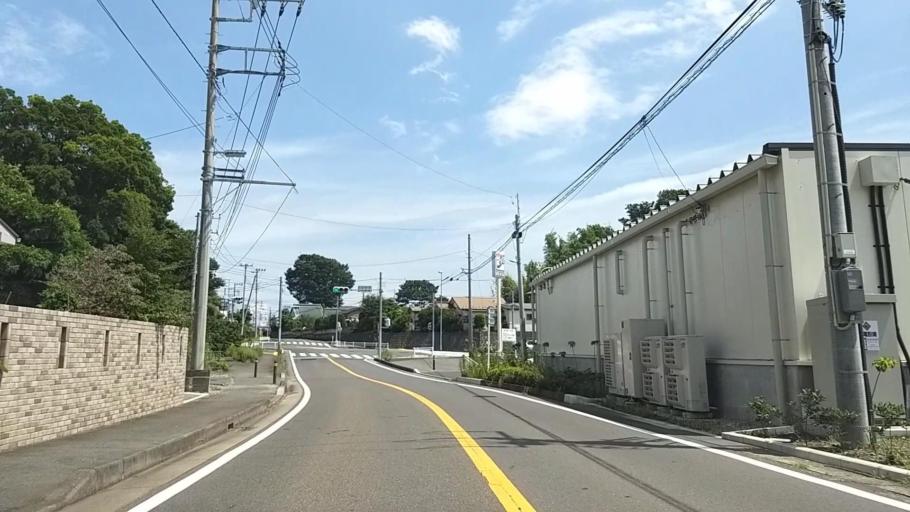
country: JP
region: Kanagawa
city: Fujisawa
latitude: 35.4065
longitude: 139.4356
